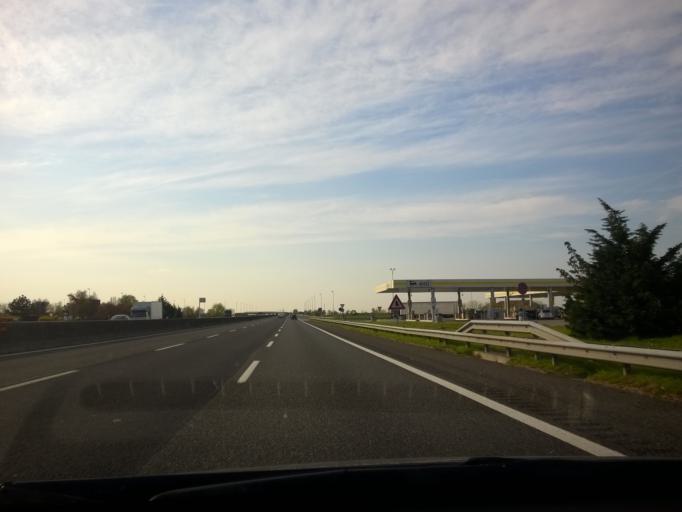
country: IT
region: Emilia-Romagna
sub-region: Forli-Cesena
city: Santa Maria Nuova
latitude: 44.2179
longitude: 12.1761
